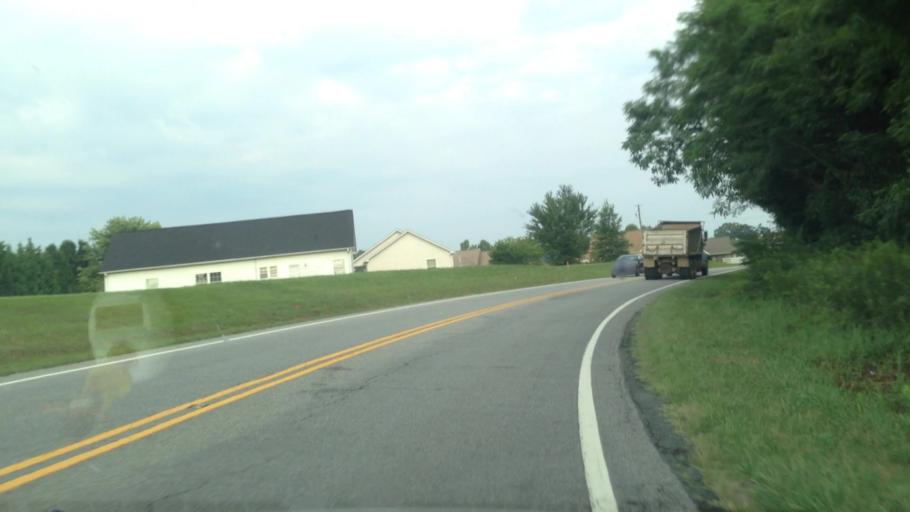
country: US
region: North Carolina
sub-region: Forsyth County
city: Walkertown
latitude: 36.1901
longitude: -80.2290
